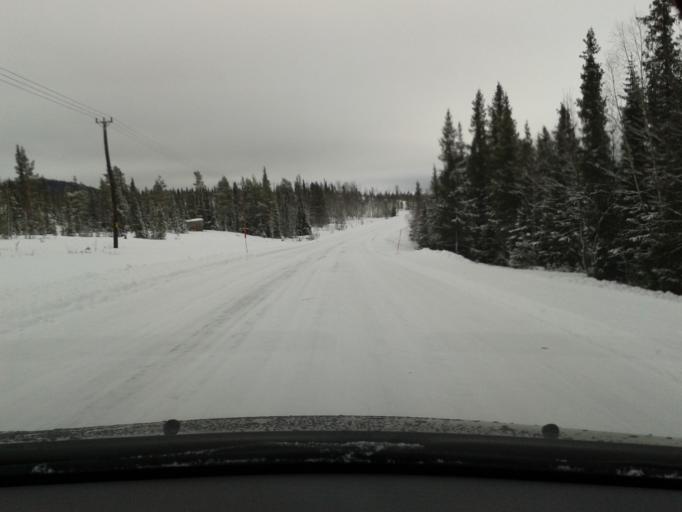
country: SE
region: Vaesterbotten
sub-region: Vilhelmina Kommun
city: Sjoberg
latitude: 65.2331
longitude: 15.8574
